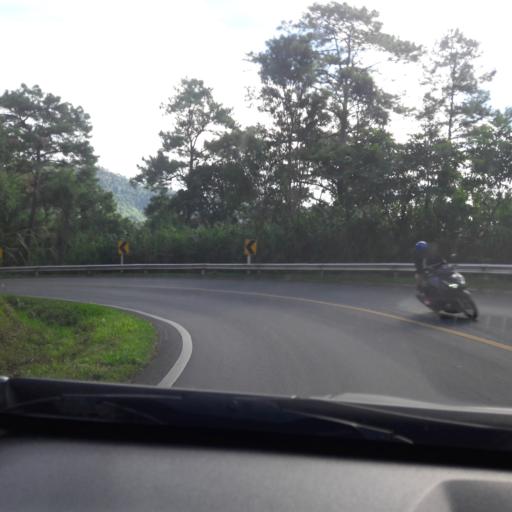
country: TH
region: Mae Hong Son
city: Sop Pong
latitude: 19.4545
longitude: 98.3090
